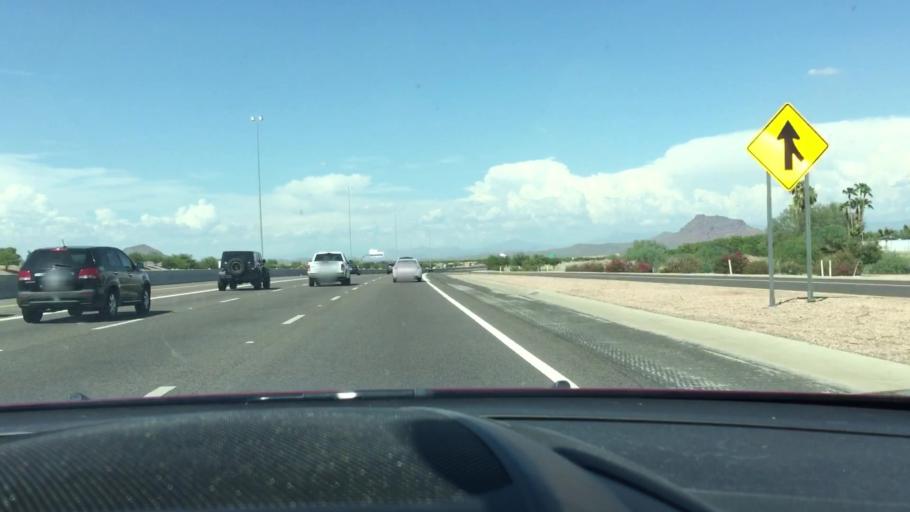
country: US
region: Arizona
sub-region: Maricopa County
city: Mesa
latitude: 33.4717
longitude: -111.7802
